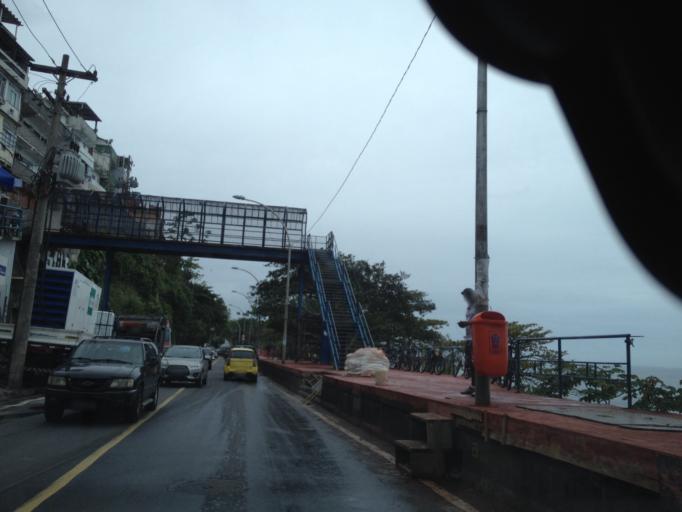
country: BR
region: Rio de Janeiro
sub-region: Rio De Janeiro
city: Rio de Janeiro
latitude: -22.9972
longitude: -43.2376
